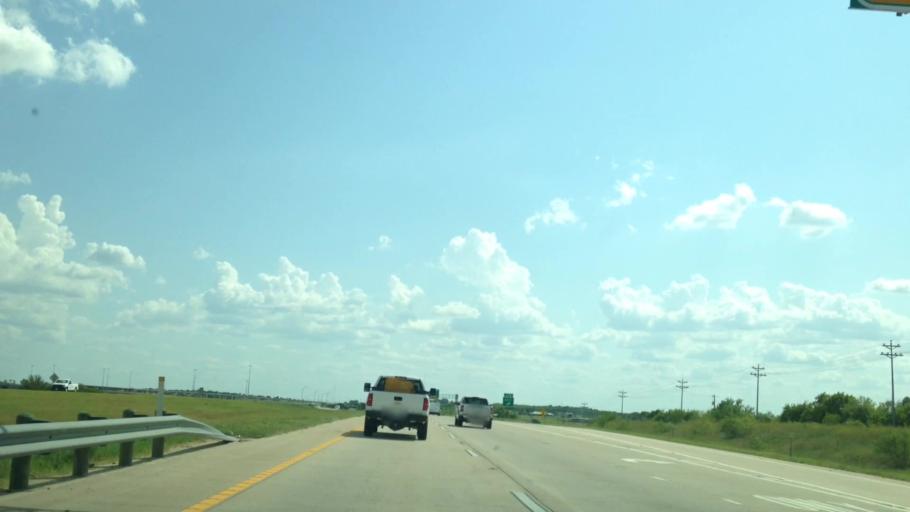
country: US
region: Texas
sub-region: Travis County
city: Manor
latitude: 30.3571
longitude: -97.5895
